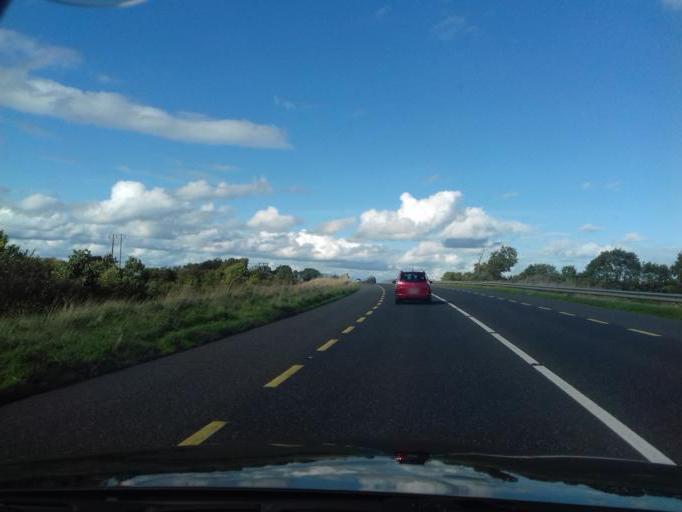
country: IE
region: Leinster
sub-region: Uibh Fhaili
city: Tullamore
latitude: 53.2596
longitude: -7.4666
